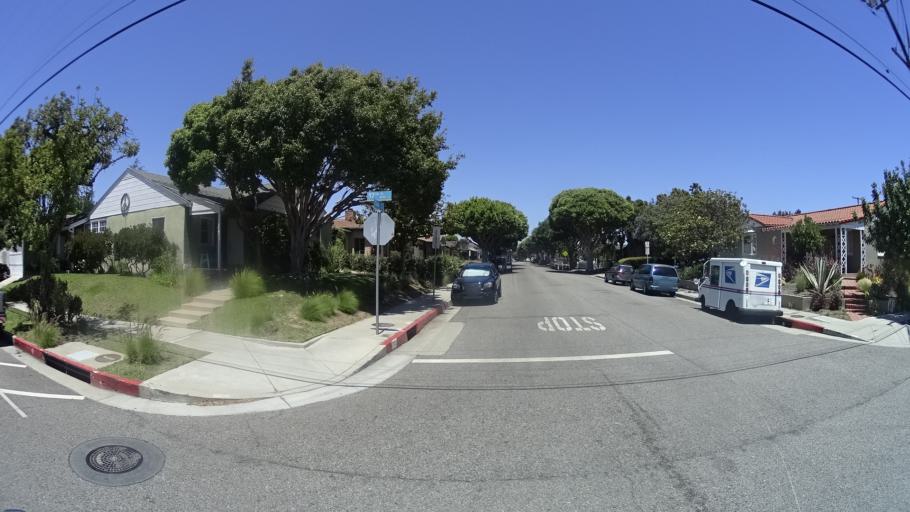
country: US
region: California
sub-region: Los Angeles County
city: Santa Monica
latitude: 34.0117
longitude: -118.4661
